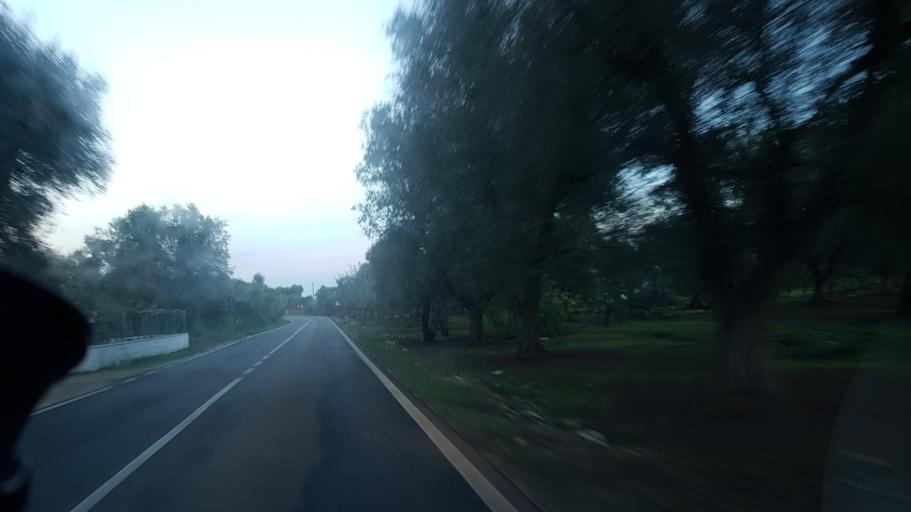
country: IT
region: Apulia
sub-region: Provincia di Brindisi
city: Latiano
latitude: 40.5687
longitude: 17.6742
